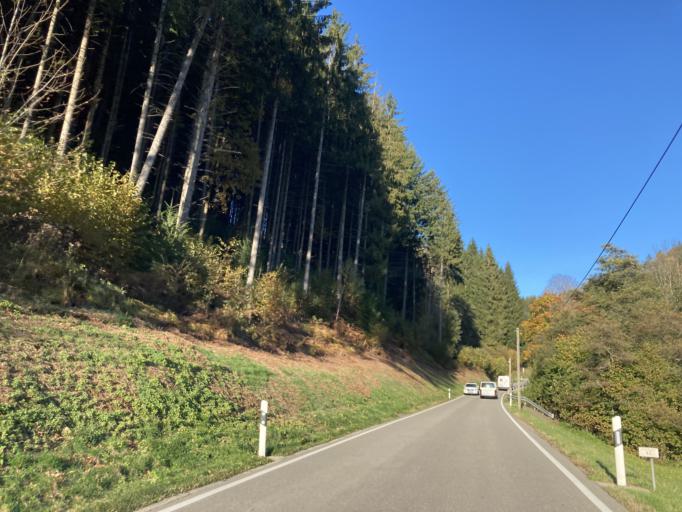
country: DE
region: Baden-Wuerttemberg
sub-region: Freiburg Region
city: Breitnau
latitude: 47.9696
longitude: 8.0858
